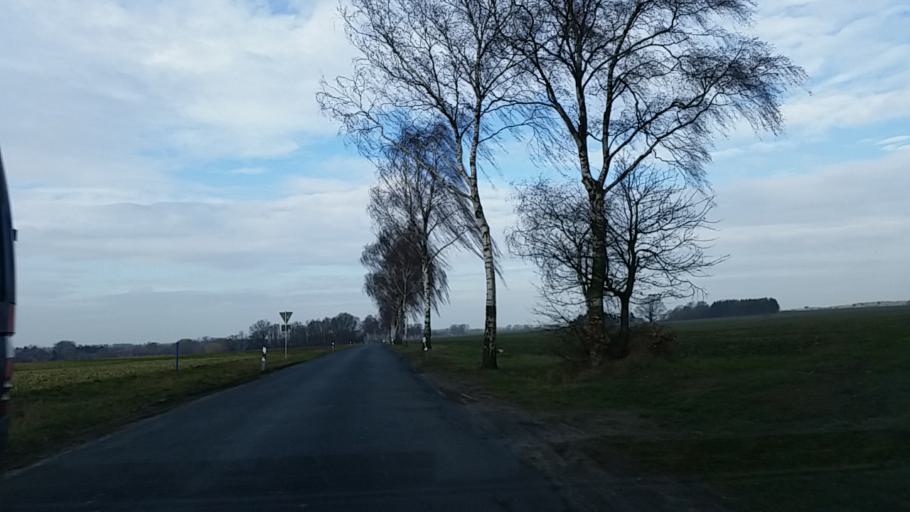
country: DE
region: Lower Saxony
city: Altenmedingen
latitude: 53.1376
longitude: 10.6332
